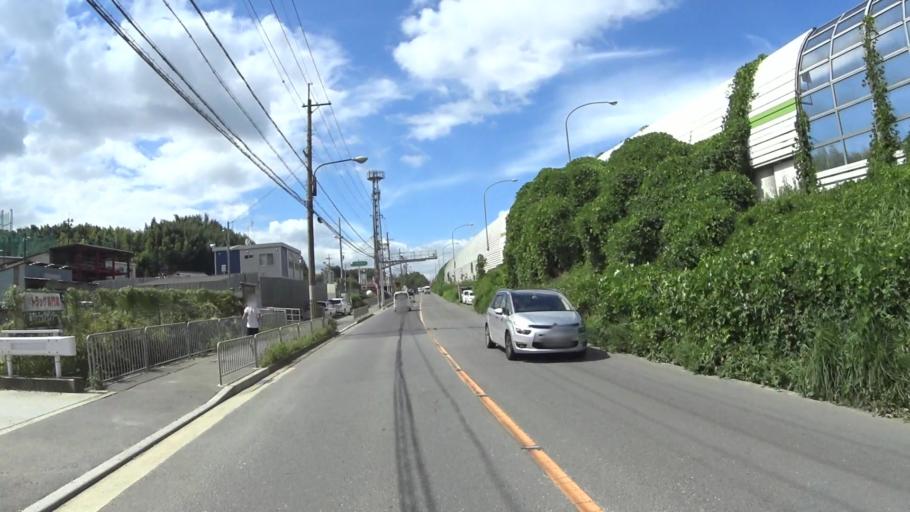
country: JP
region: Kyoto
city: Uji
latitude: 34.9565
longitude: 135.7941
